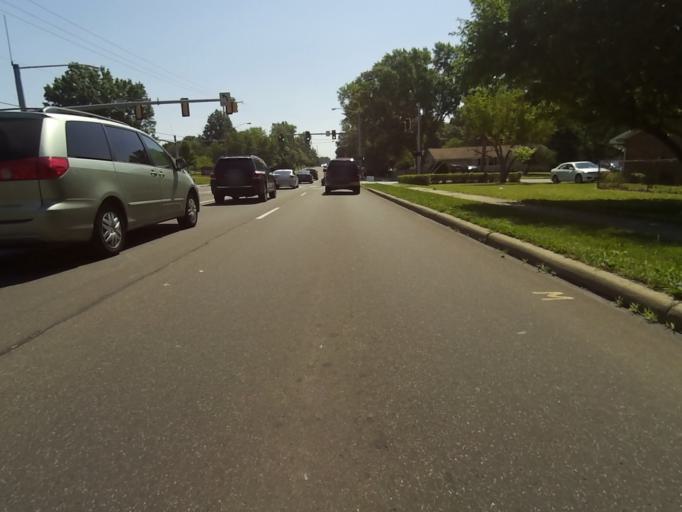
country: US
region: Ohio
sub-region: Summit County
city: Silver Lake
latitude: 41.1667
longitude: -81.4491
